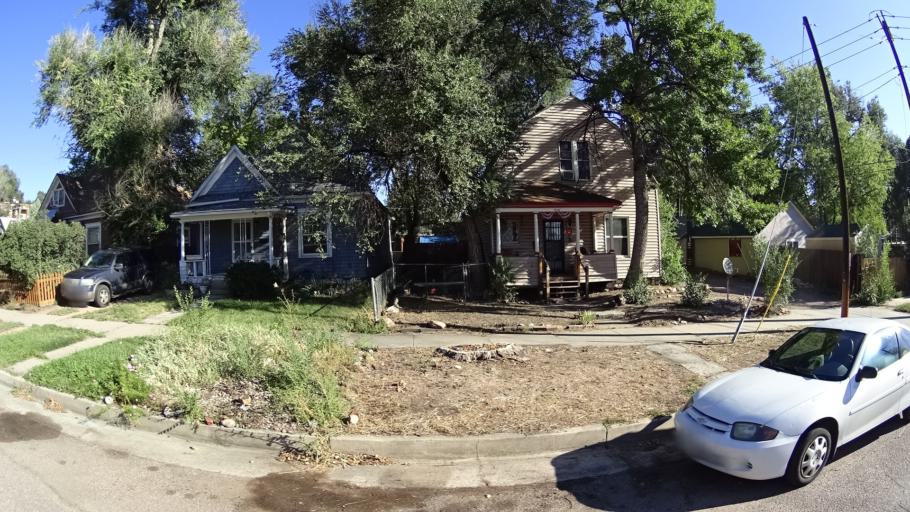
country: US
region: Colorado
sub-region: El Paso County
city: Colorado Springs
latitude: 38.8391
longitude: -104.8343
